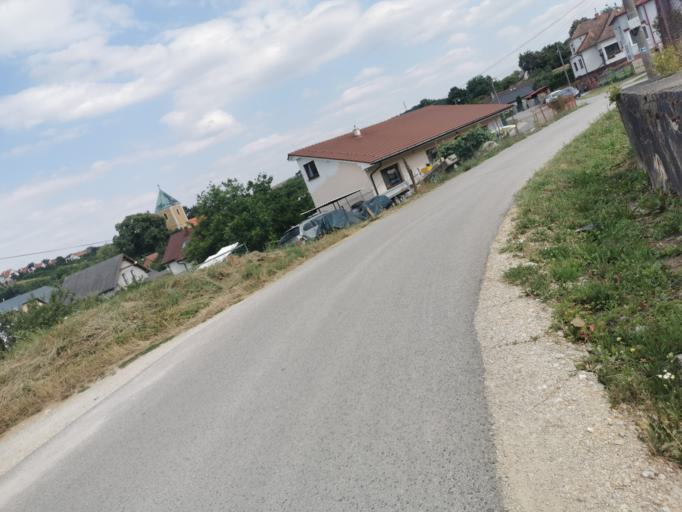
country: SK
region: Trenciansky
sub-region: Okres Myjava
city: Myjava
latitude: 48.7448
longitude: 17.5309
